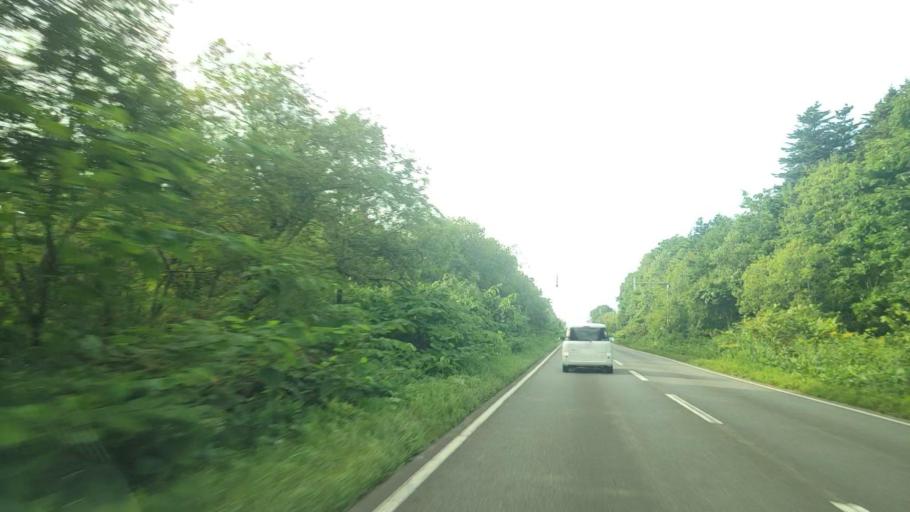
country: JP
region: Hokkaido
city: Makubetsu
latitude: 45.0503
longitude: 141.7511
